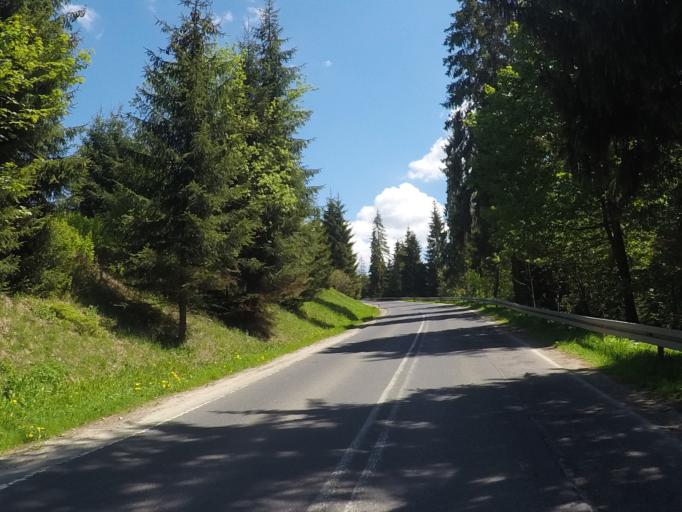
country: PL
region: Lesser Poland Voivodeship
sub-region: Powiat tatrzanski
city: Bukowina Tatrzanska
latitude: 49.3330
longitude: 20.0808
